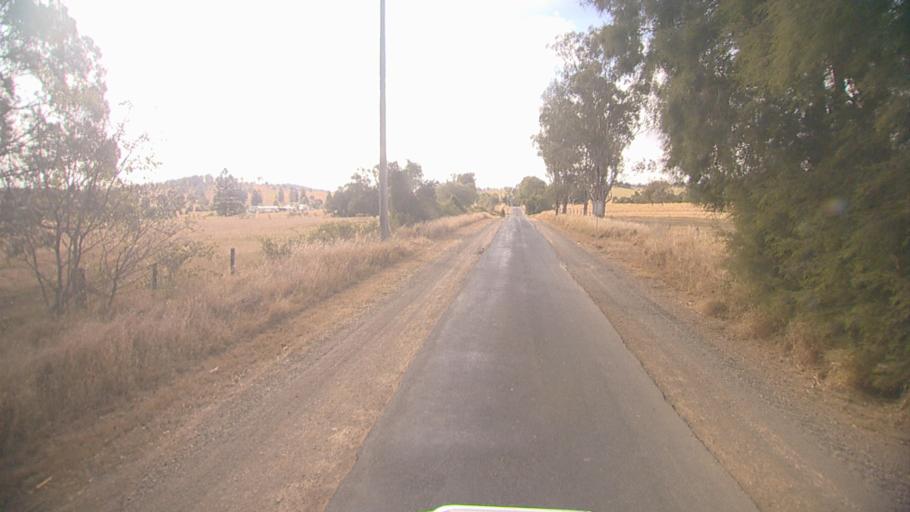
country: AU
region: Queensland
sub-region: Logan
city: Cedar Vale
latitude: -27.9190
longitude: 153.0130
